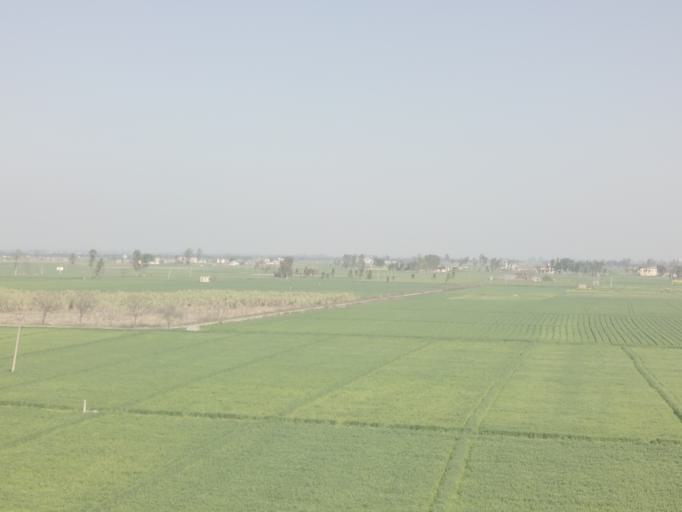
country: IN
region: Punjab
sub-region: Shahid Bhagat Singh Nagar
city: Rahon
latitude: 31.0242
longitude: 76.0931
